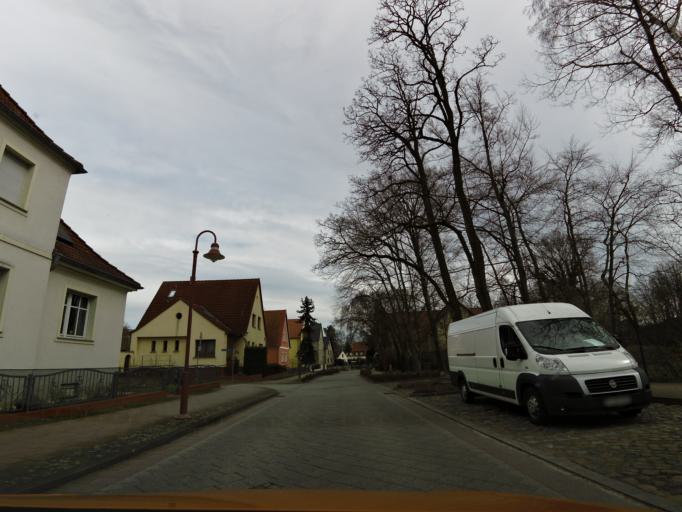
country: DE
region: Brandenburg
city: Belzig
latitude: 52.1469
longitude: 12.5909
